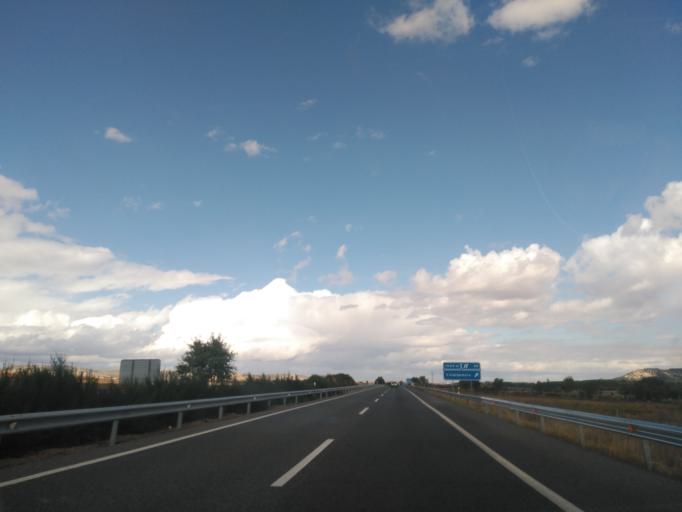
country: ES
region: Castille and Leon
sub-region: Provincia de Burgos
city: Villaquiran de los Infantes
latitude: 42.2273
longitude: -3.9949
